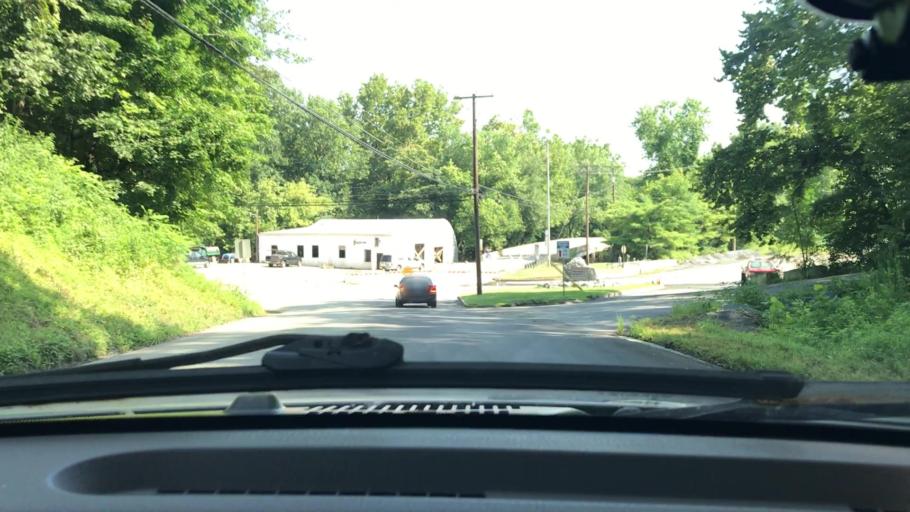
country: US
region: Pennsylvania
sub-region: Dauphin County
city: Hummelstown
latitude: 40.2484
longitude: -76.7366
